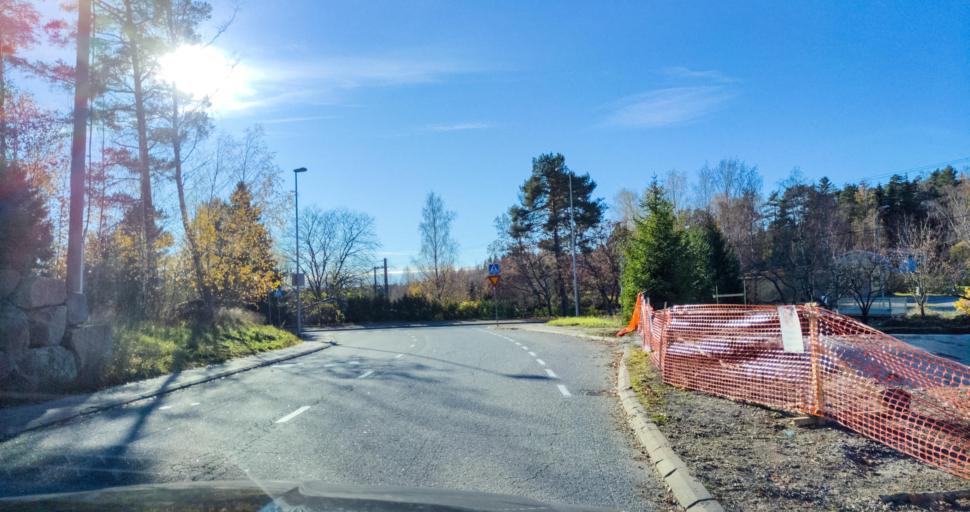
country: FI
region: Varsinais-Suomi
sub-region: Turku
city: Turku
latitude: 60.3946
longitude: 22.2042
